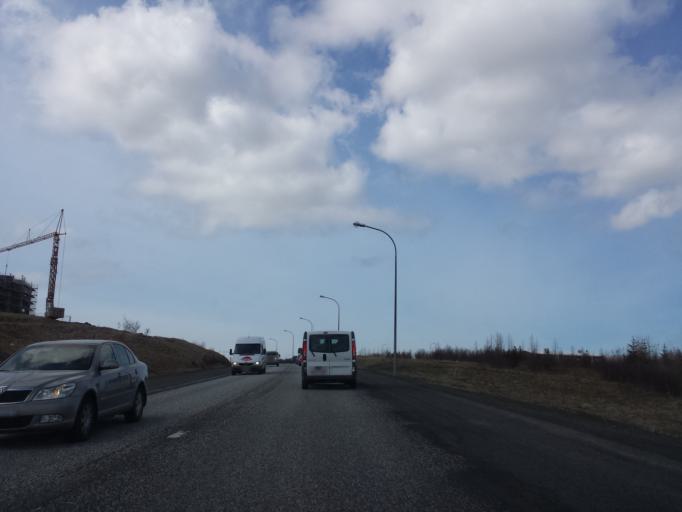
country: IS
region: Capital Region
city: Reykjavik
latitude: 64.0978
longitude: -21.8094
